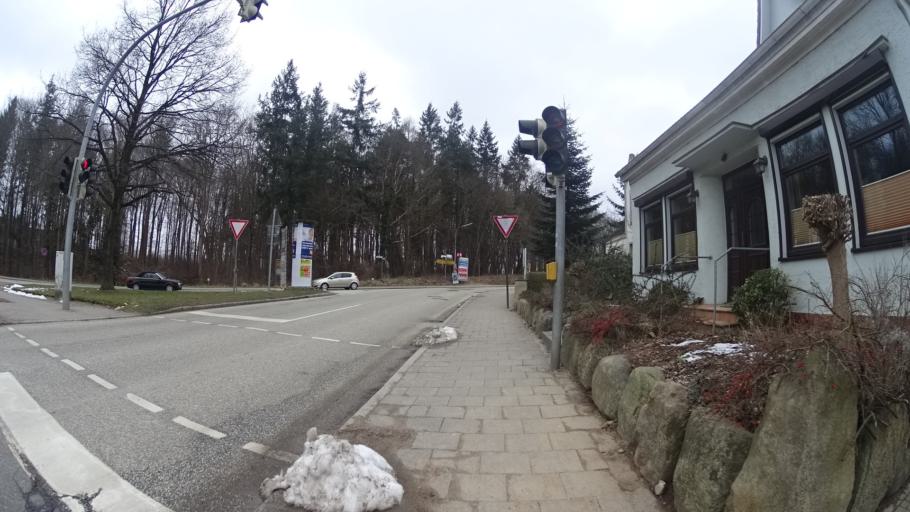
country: DE
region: Schleswig-Holstein
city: Malente
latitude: 54.1795
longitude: 10.5626
